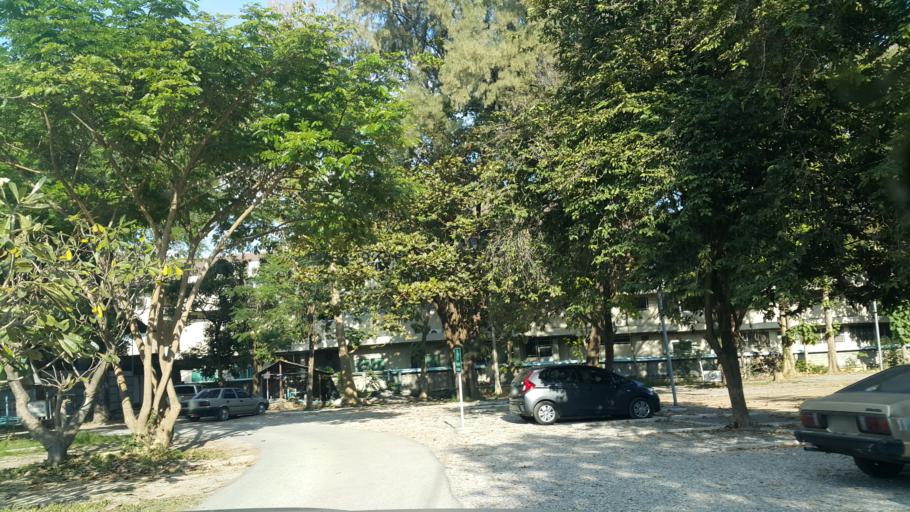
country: TH
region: Chiang Mai
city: Chiang Mai
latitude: 18.7965
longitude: 99.0114
